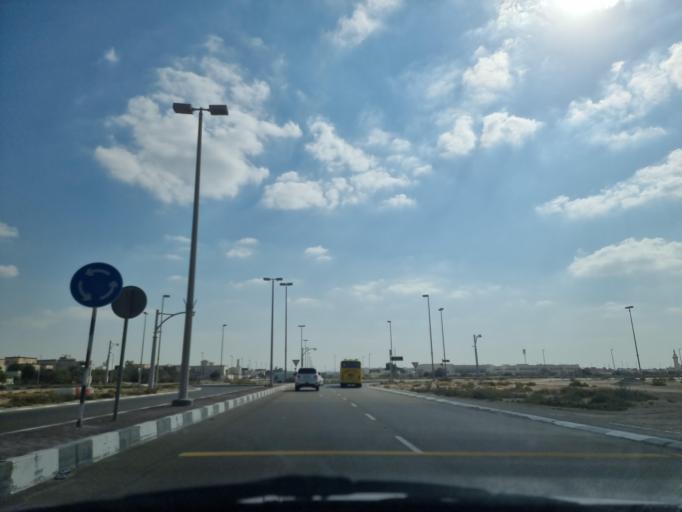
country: AE
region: Abu Dhabi
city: Abu Dhabi
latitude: 24.4139
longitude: 54.7326
